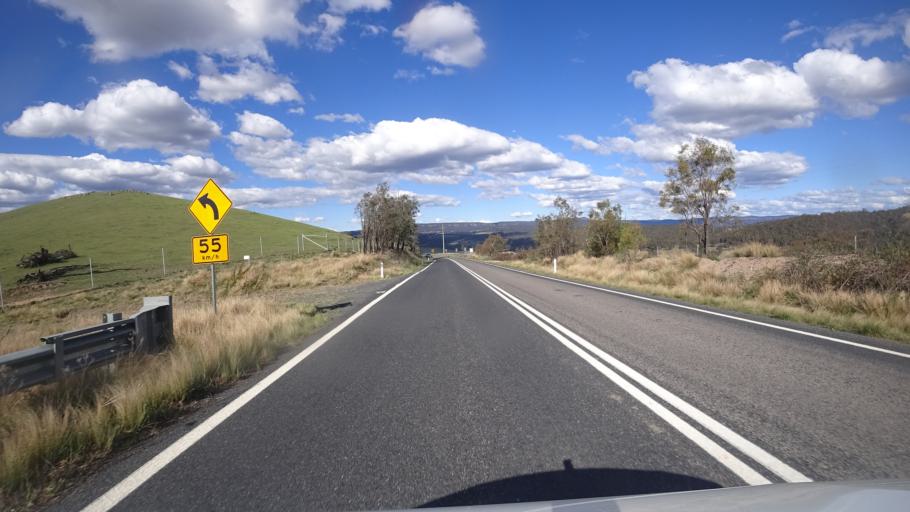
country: AU
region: New South Wales
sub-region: Lithgow
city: Bowenfels
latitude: -33.5673
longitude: 150.1281
